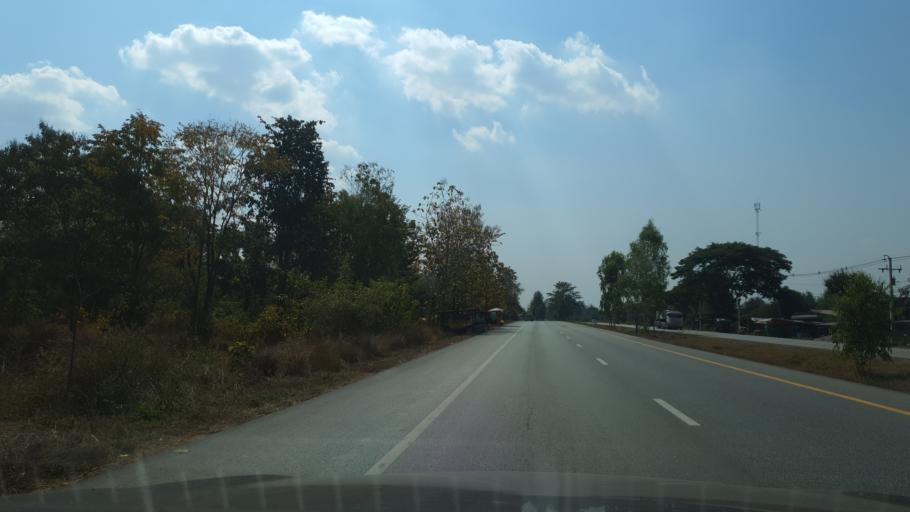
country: TH
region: Tak
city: Sam Ngao
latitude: 17.2986
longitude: 99.1448
